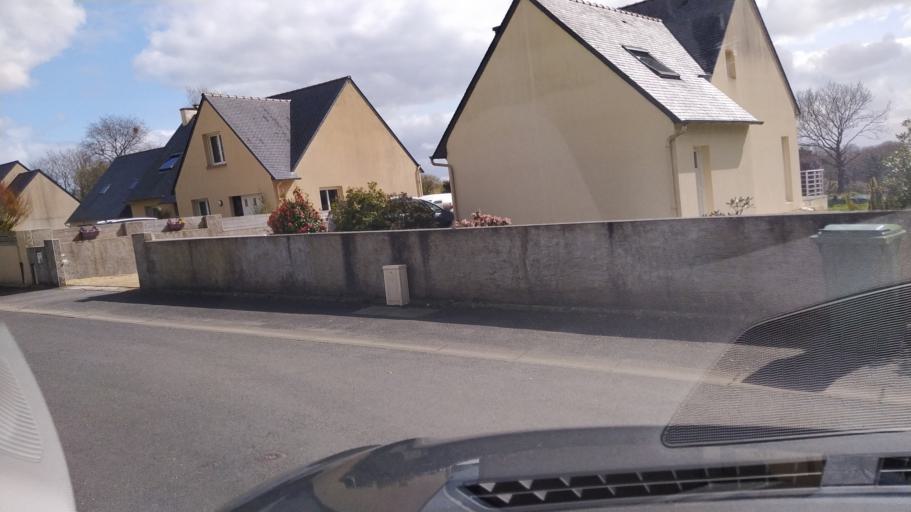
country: FR
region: Brittany
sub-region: Departement du Finistere
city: Bodilis
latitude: 48.5281
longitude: -4.1120
